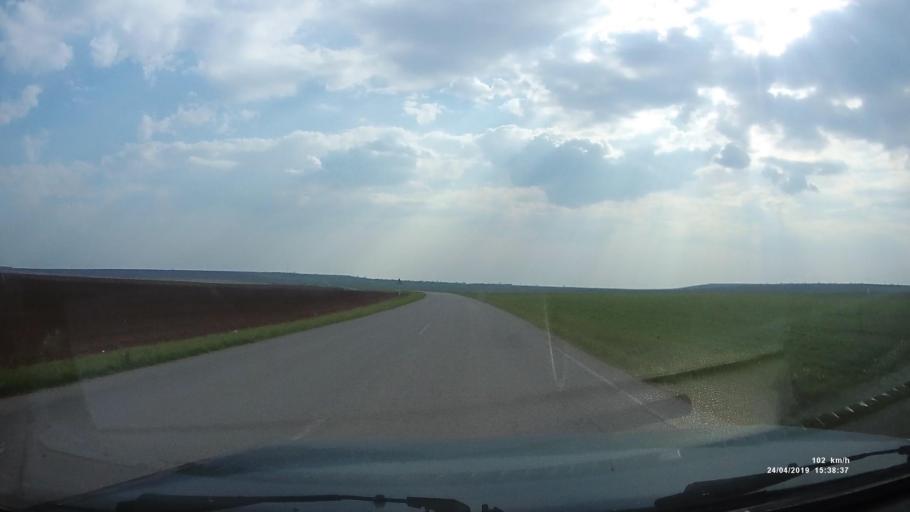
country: RU
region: Kalmykiya
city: Yashalta
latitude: 46.5959
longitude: 42.8249
